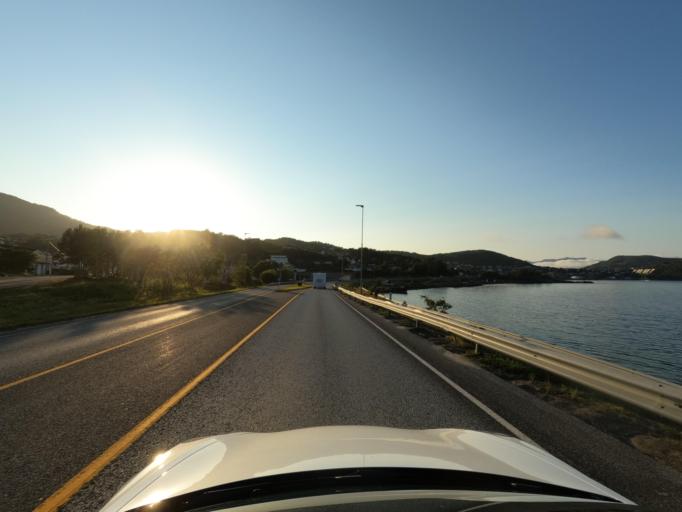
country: NO
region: Troms
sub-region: Harstad
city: Harstad
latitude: 68.7615
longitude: 16.5632
